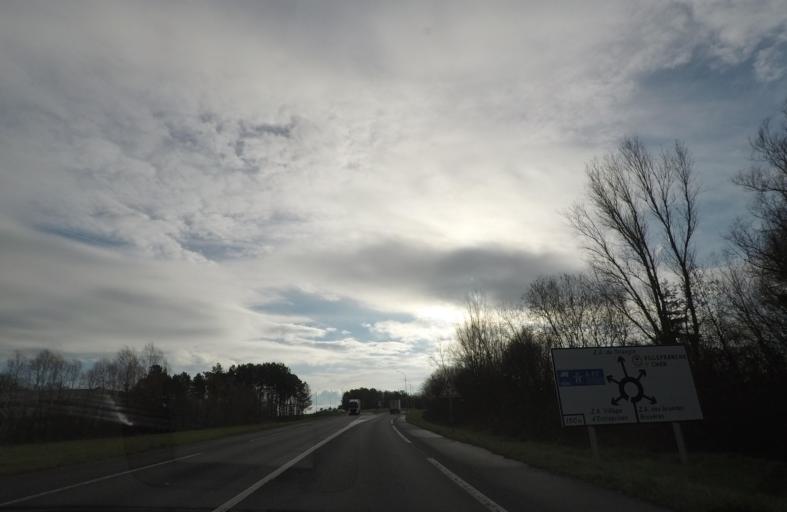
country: FR
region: Centre
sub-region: Departement du Loir-et-Cher
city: Villefranche-sur-Cher
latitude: 47.3289
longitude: 1.7604
